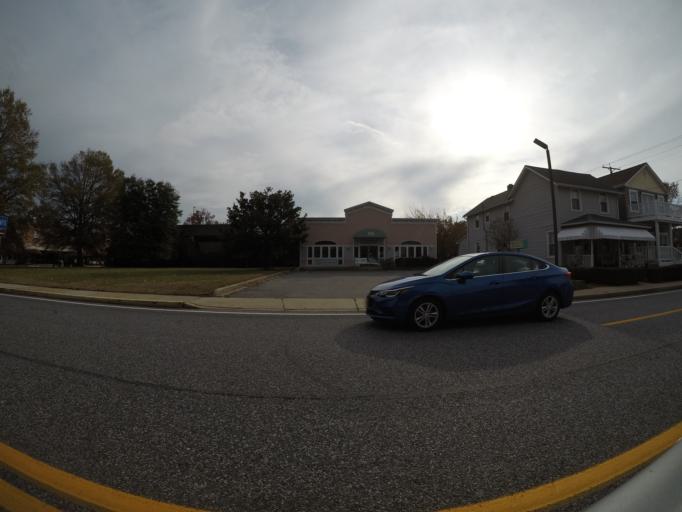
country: US
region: Maryland
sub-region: Harford County
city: Havre de Grace
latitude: 39.5430
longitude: -76.0924
